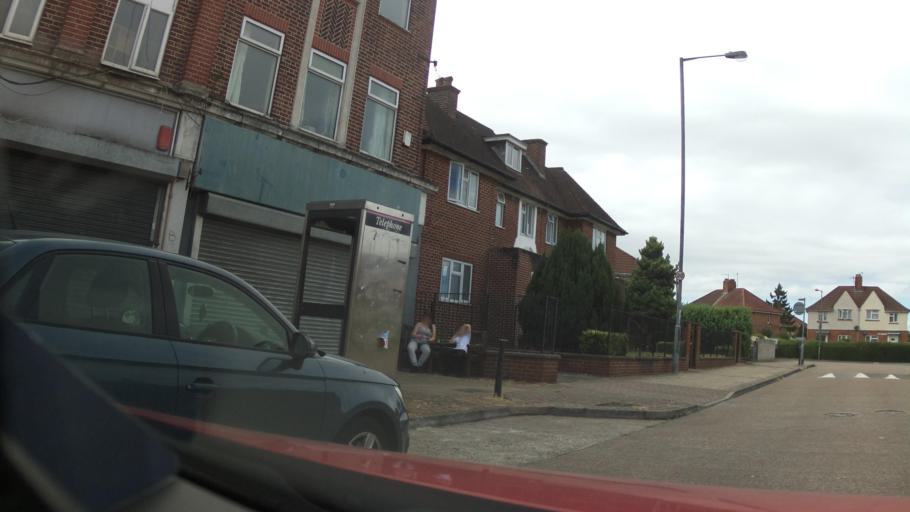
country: GB
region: England
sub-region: Bath and North East Somerset
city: Whitchurch
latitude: 51.4249
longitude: -2.5858
